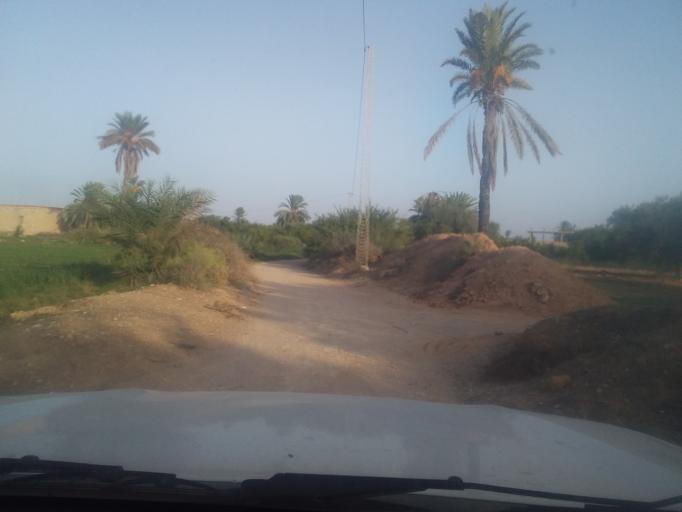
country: TN
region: Qabis
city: Gabes
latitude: 33.6313
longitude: 10.2941
